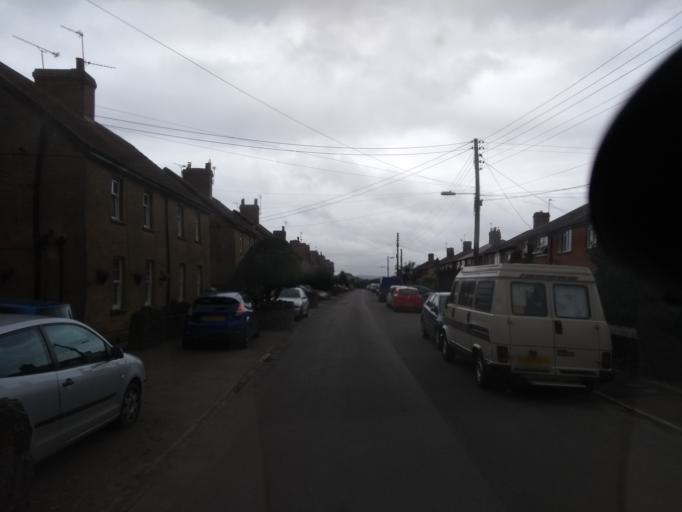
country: GB
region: England
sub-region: Somerset
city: Stoke-sub-Hamdon
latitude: 50.9498
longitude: -2.7556
